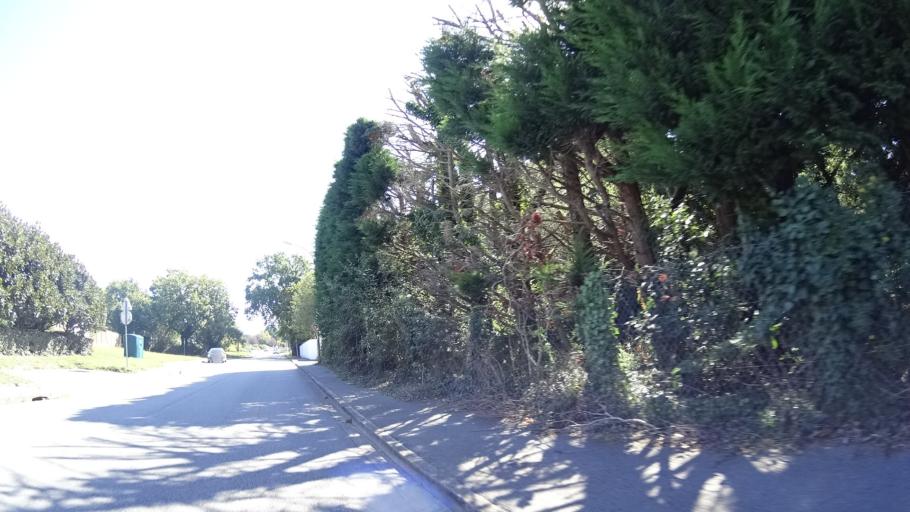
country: FR
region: Brittany
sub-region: Departement du Morbihan
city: Vannes
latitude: 47.6430
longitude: -2.7577
